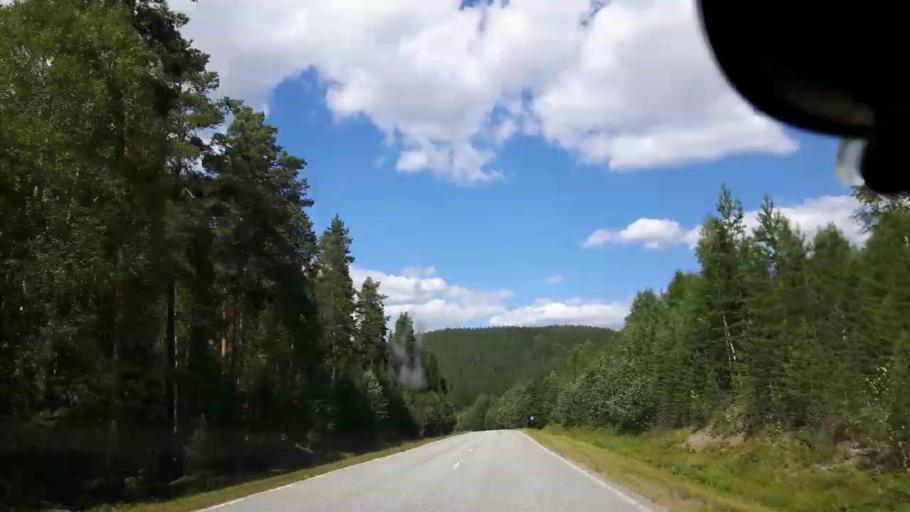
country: SE
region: Vaesternorrland
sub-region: Ange Kommun
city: Fransta
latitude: 62.7345
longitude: 16.3302
